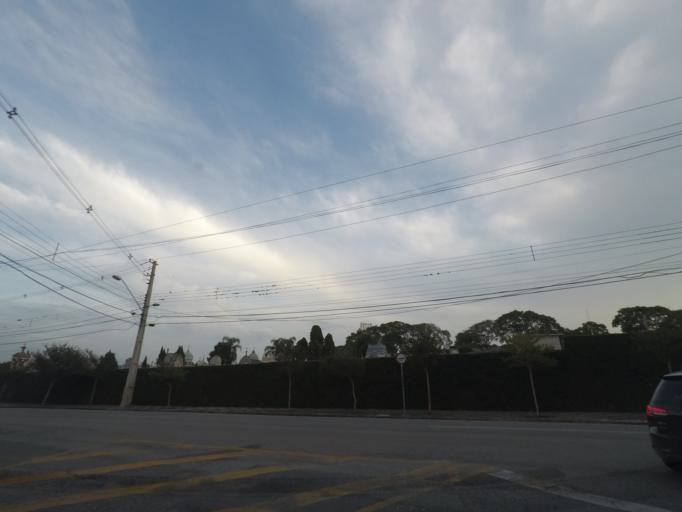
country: BR
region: Parana
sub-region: Curitiba
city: Curitiba
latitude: -25.4189
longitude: -49.2763
